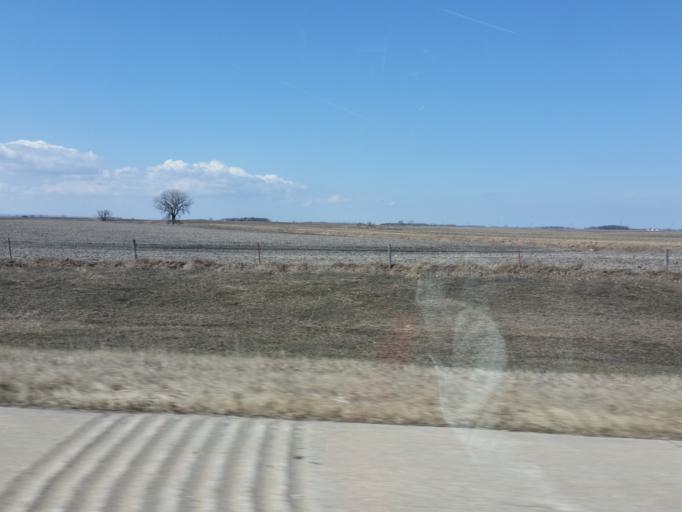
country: US
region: South Dakota
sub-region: Roberts County
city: Sisseton
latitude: 45.7751
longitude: -96.9075
